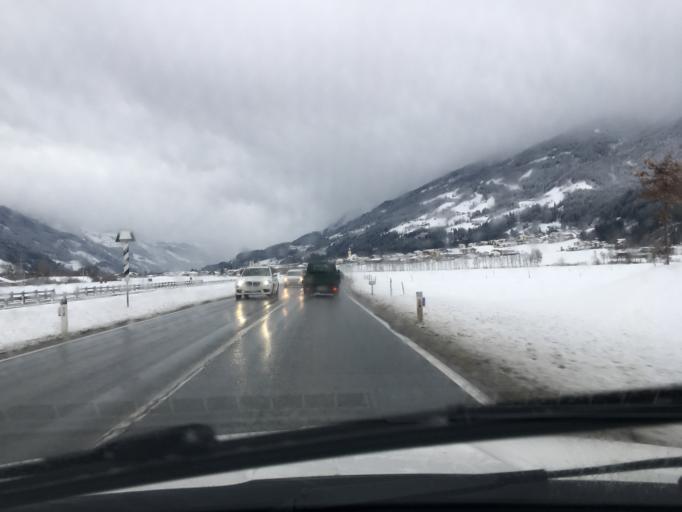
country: AT
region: Tyrol
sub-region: Politischer Bezirk Schwaz
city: Uderns
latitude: 47.3148
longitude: 11.8663
